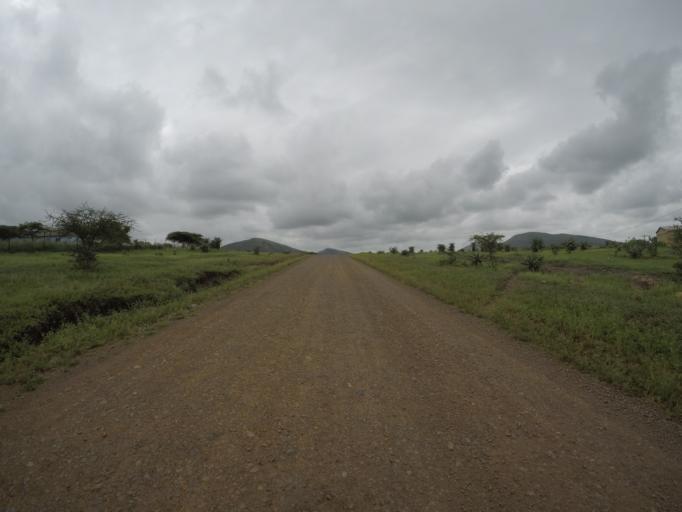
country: ZA
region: KwaZulu-Natal
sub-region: uThungulu District Municipality
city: Empangeni
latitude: -28.6093
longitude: 31.8674
